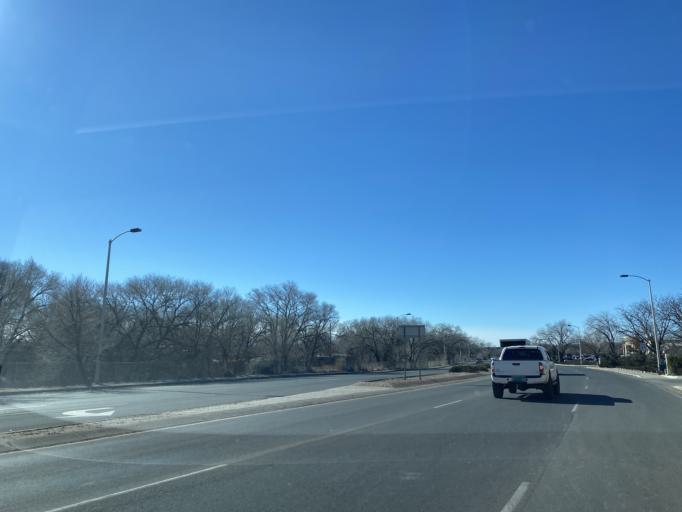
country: US
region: New Mexico
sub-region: Santa Fe County
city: Santa Fe
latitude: 35.6923
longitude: -105.9479
